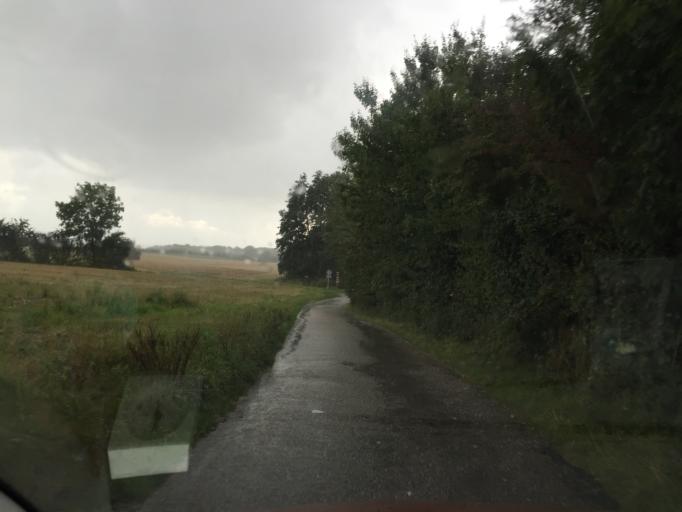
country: DK
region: South Denmark
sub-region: Sonderborg Kommune
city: Dybbol
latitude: 54.9454
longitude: 9.7503
